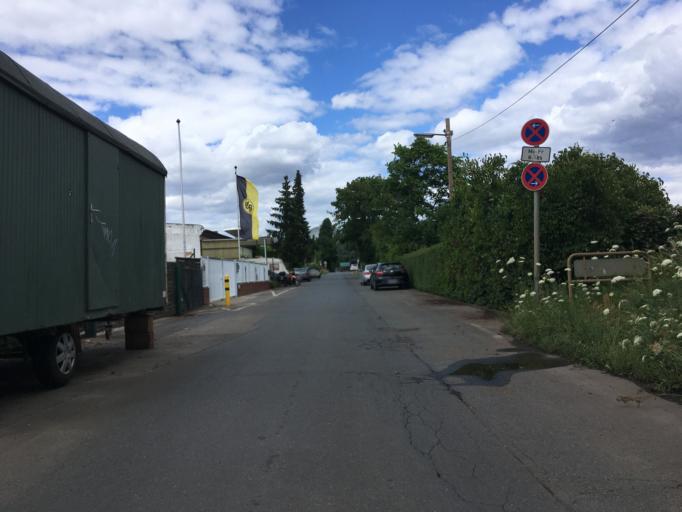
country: DE
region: Berlin
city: Mariendorf
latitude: 52.4337
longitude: 13.3709
